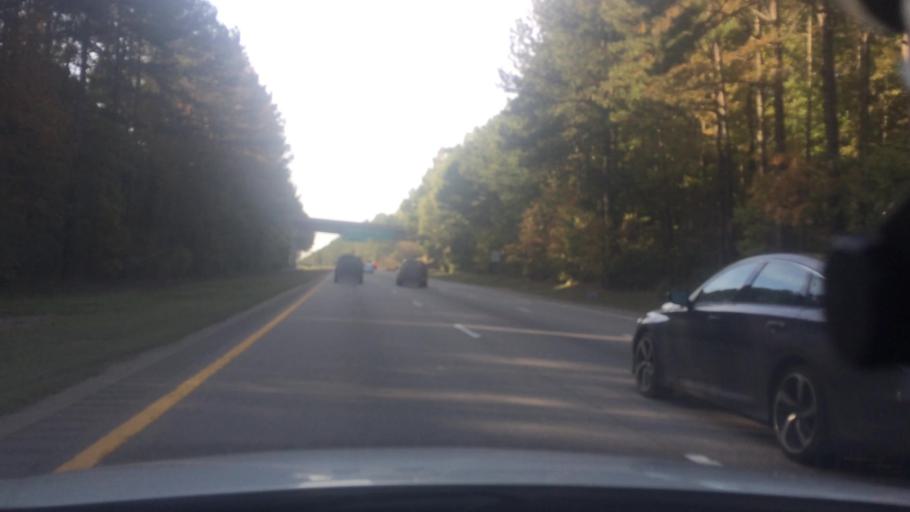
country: US
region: North Carolina
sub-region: Wake County
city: Cary
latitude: 35.8165
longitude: -78.7366
